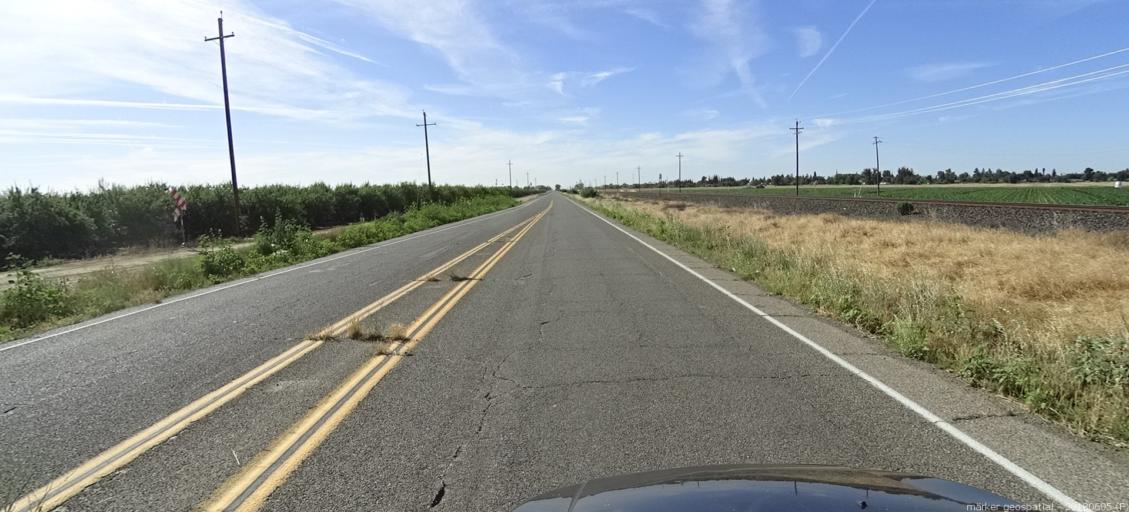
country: US
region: California
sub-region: Madera County
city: Chowchilla
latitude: 37.1348
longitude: -120.2691
